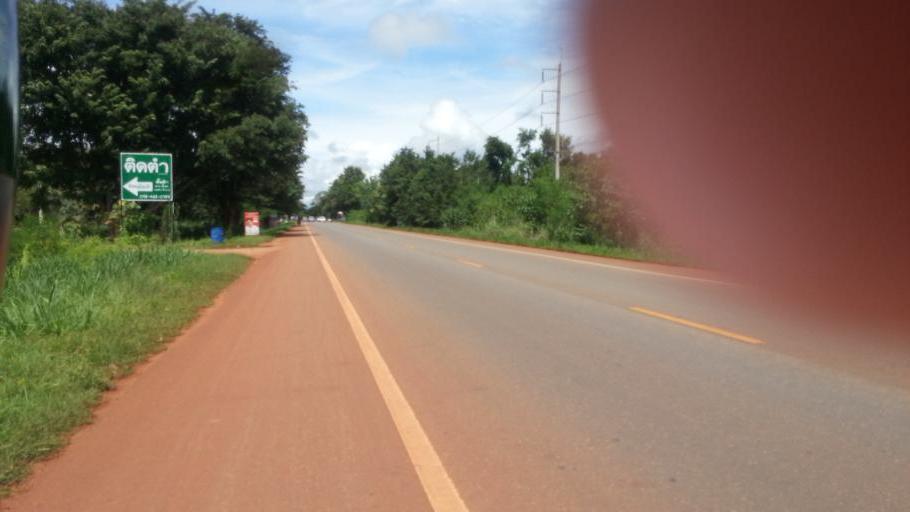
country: TH
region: Kanchanaburi
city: Sai Yok
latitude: 14.1210
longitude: 99.1806
